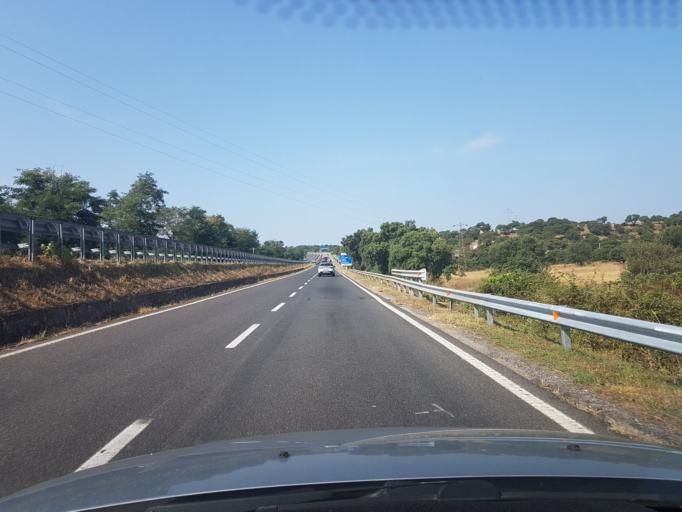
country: IT
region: Sardinia
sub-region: Provincia di Nuoro
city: Oniferi
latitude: 40.3085
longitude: 9.1982
